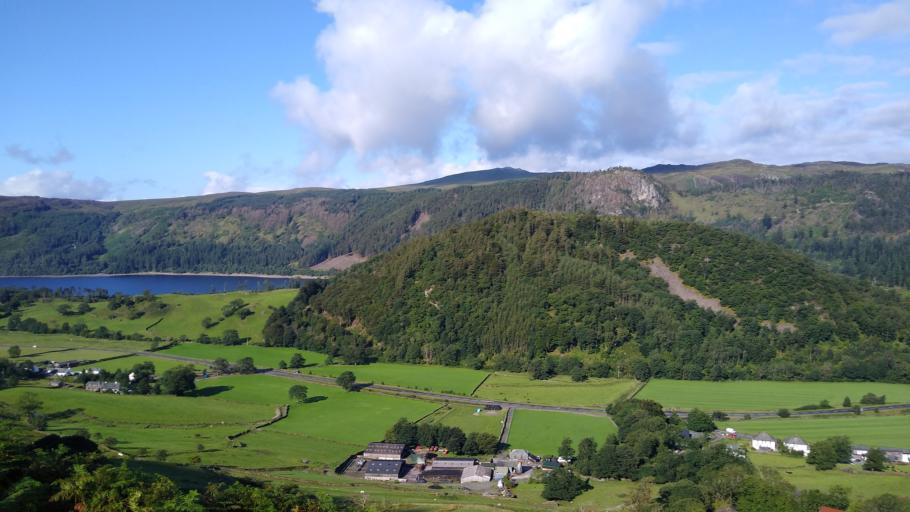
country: GB
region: England
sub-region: Cumbria
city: Keswick
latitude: 54.5610
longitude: -3.0479
